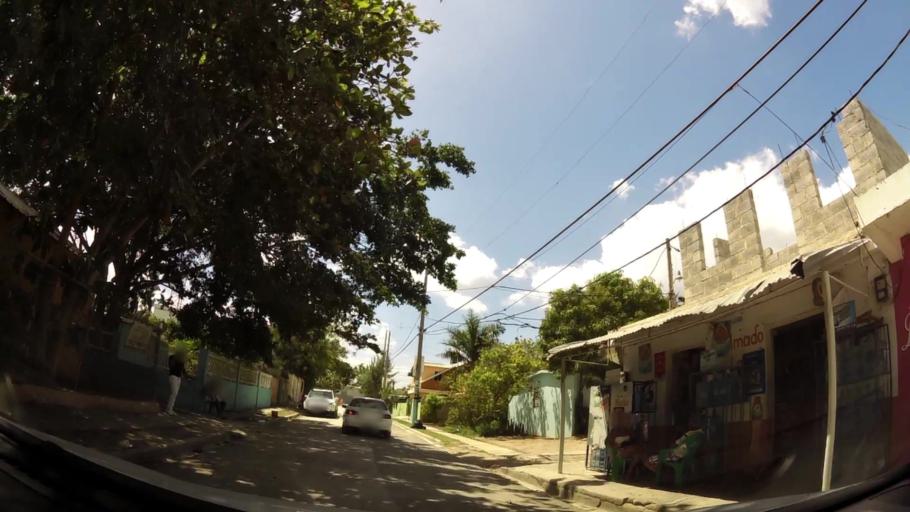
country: DO
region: Santo Domingo
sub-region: Santo Domingo
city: Boca Chica
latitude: 18.4500
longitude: -69.6547
